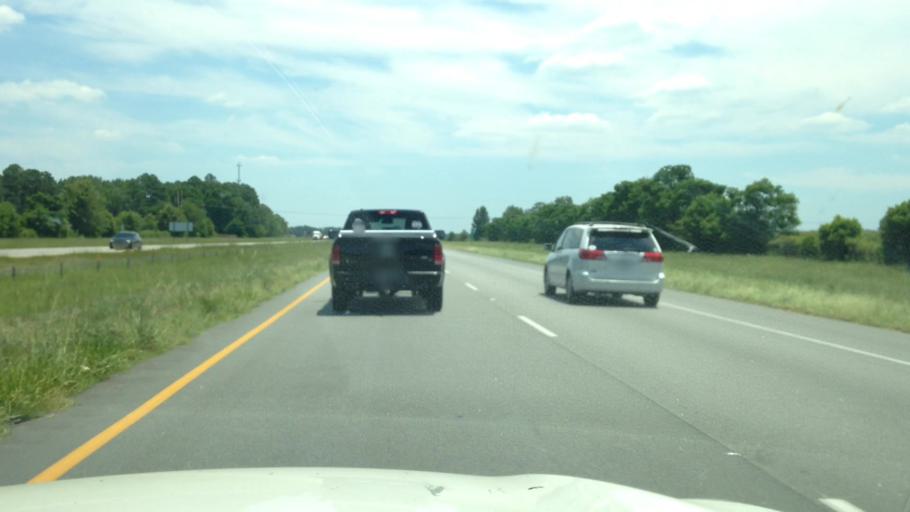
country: US
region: South Carolina
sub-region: Lee County
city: Bishopville
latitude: 34.1870
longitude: -80.2306
